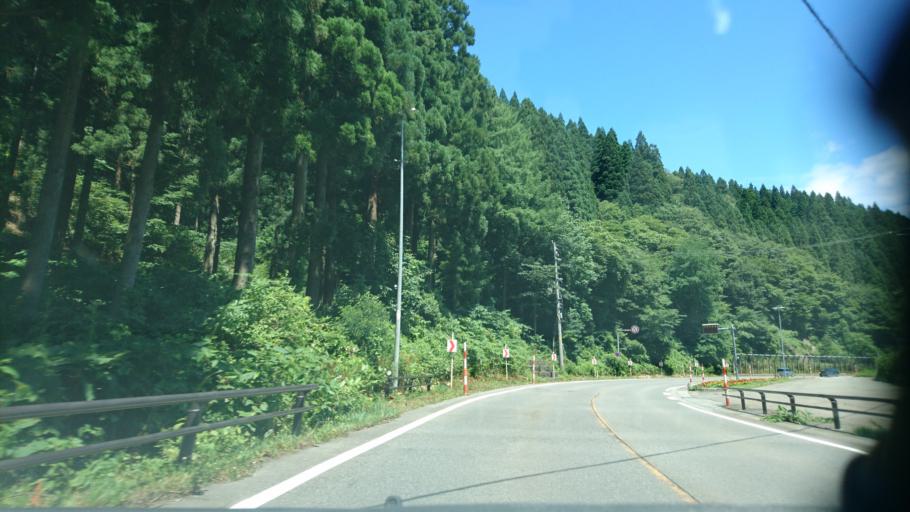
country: JP
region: Akita
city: Kakunodatemachi
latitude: 39.6419
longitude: 140.6605
